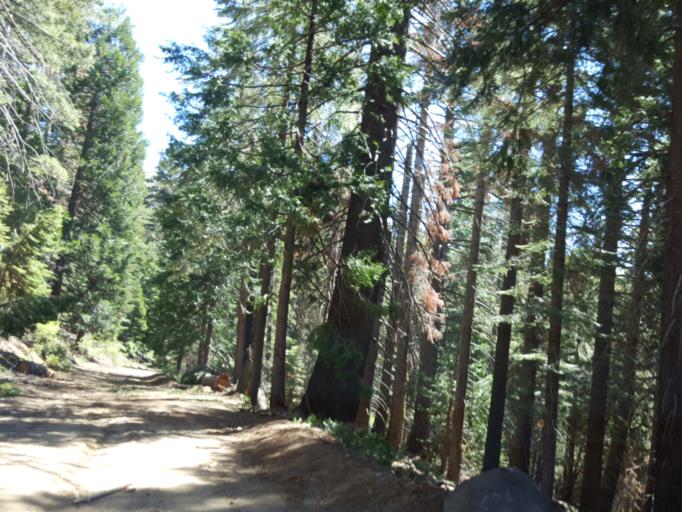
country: US
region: California
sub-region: Madera County
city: Oakhurst
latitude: 37.3731
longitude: -119.4916
